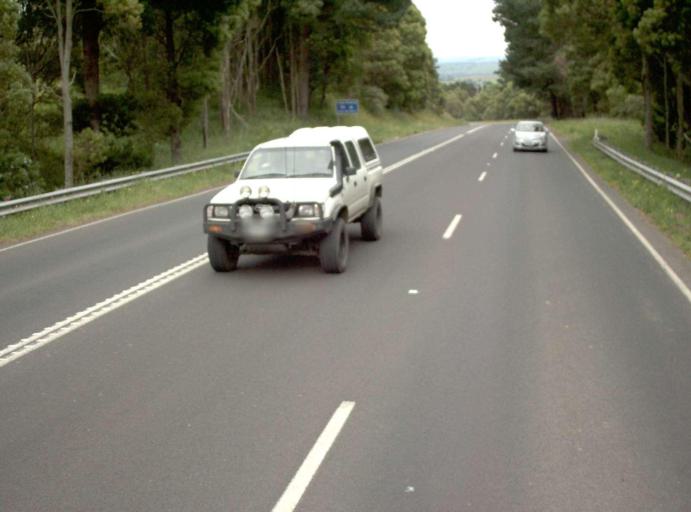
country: AU
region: Victoria
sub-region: Latrobe
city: Morwell
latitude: -38.6189
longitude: 146.1674
